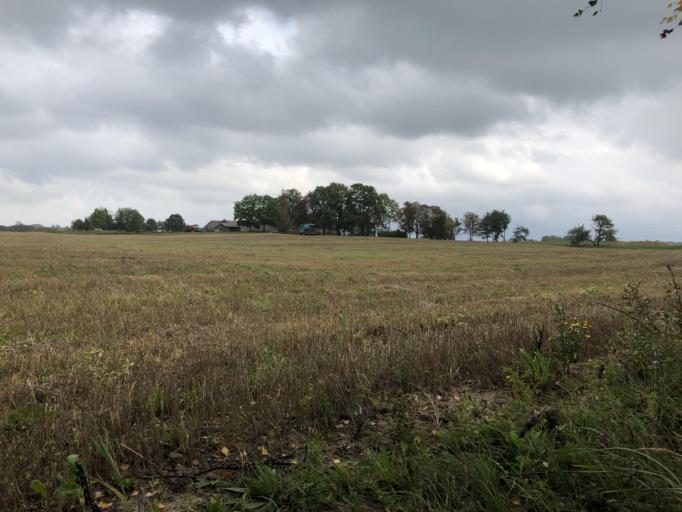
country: LV
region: Talsu Rajons
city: Sabile
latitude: 56.9702
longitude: 22.4013
